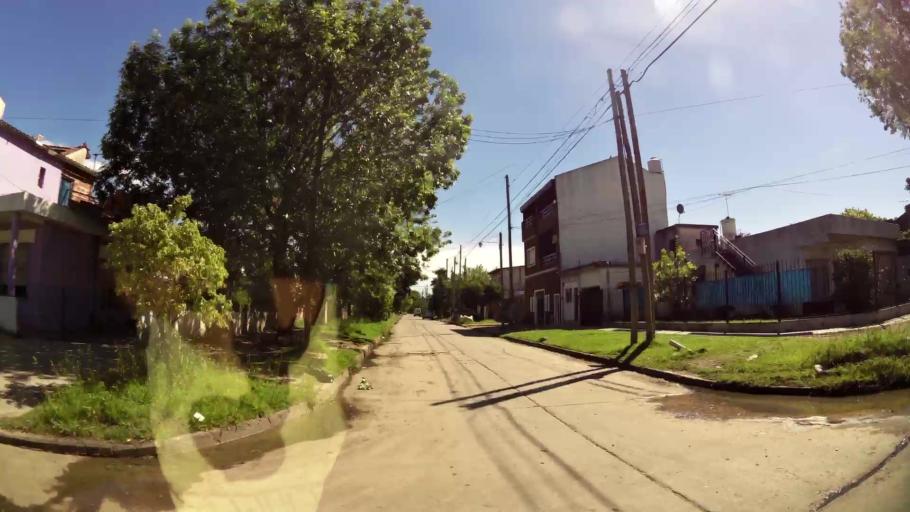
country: AR
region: Buenos Aires
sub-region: Partido de Almirante Brown
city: Adrogue
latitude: -34.7678
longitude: -58.3582
